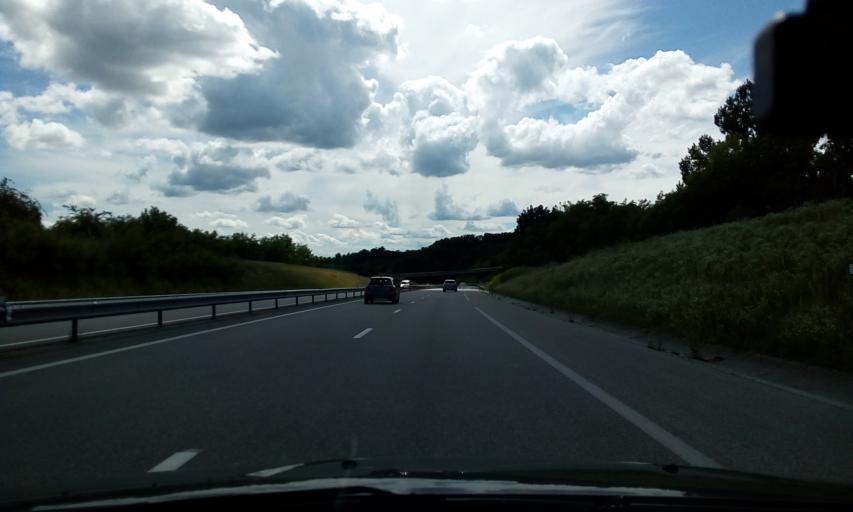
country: FR
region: Rhone-Alpes
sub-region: Departement de l'Isere
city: Saint-Hilaire-du-Rosier
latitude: 45.1167
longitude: 5.2646
